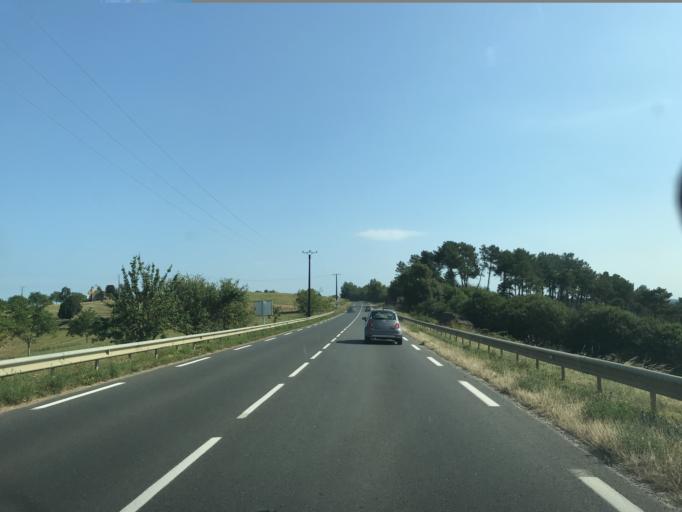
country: FR
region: Aquitaine
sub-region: Departement de la Dordogne
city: Sarlat-la-Caneda
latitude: 44.9454
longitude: 1.2213
